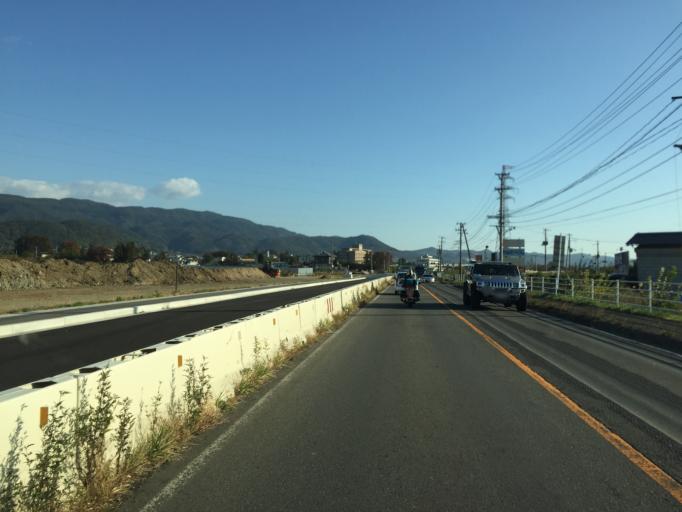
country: JP
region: Fukushima
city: Hobaramachi
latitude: 37.8673
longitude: 140.5346
